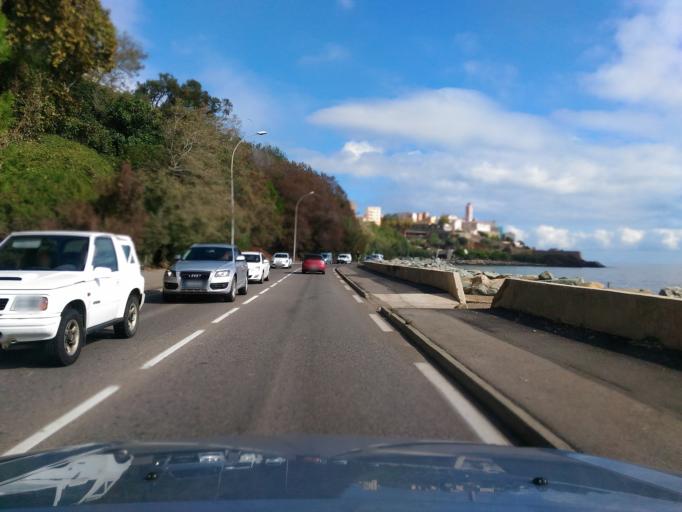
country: FR
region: Corsica
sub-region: Departement de la Haute-Corse
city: Bastia
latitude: 42.6877
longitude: 9.4469
